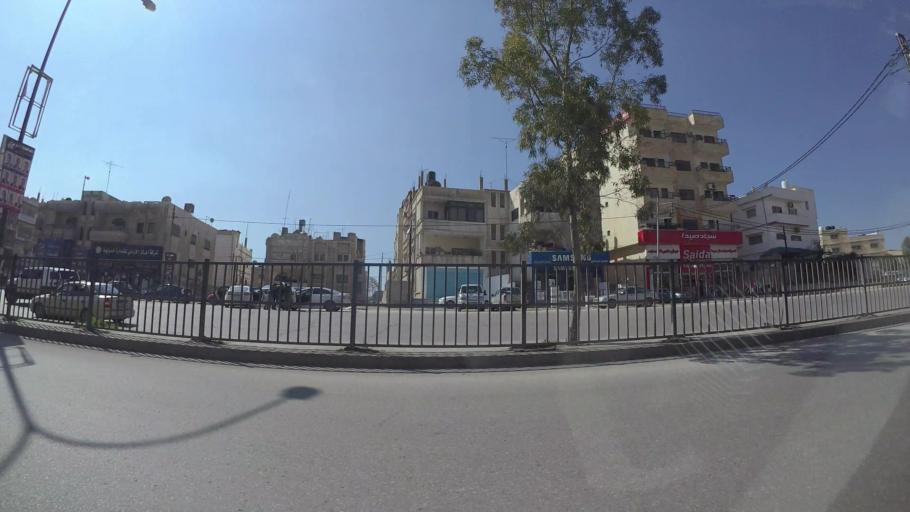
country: JO
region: Zarqa
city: Zarqa
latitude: 32.0486
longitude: 36.0928
